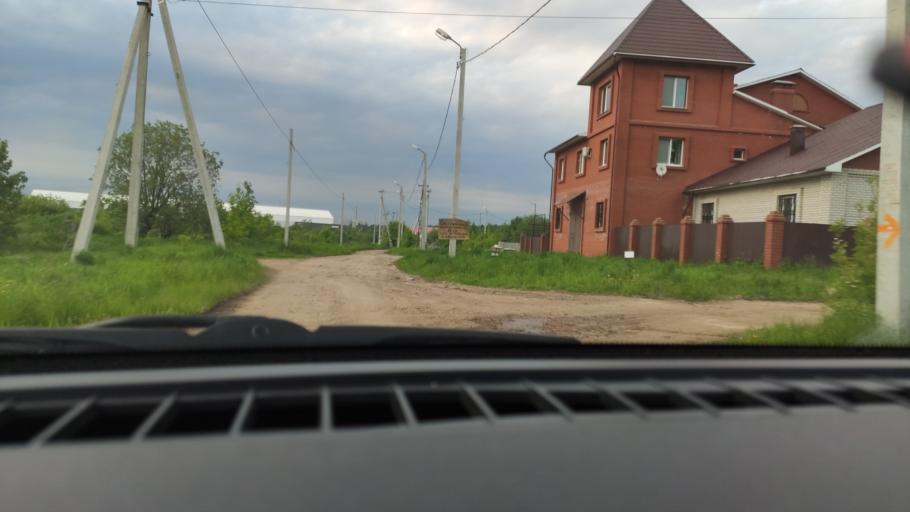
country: RU
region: Perm
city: Froly
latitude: 57.9536
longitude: 56.2850
